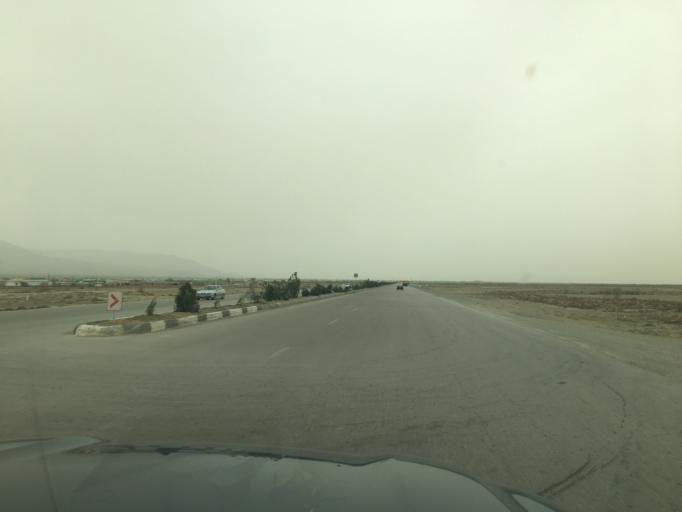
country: TM
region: Ahal
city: Baharly
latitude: 38.3766
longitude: 57.5083
